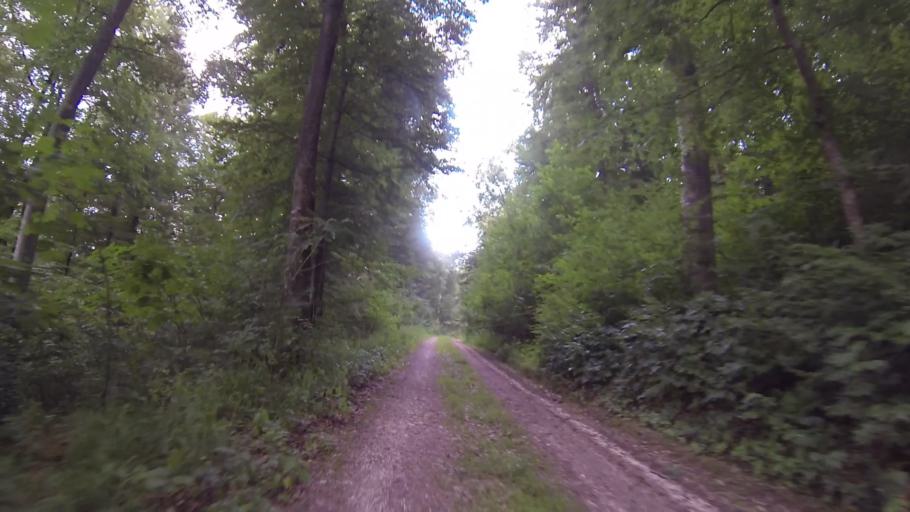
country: DE
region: Baden-Wuerttemberg
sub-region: Tuebingen Region
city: Dornstadt
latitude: 48.4406
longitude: 9.8725
